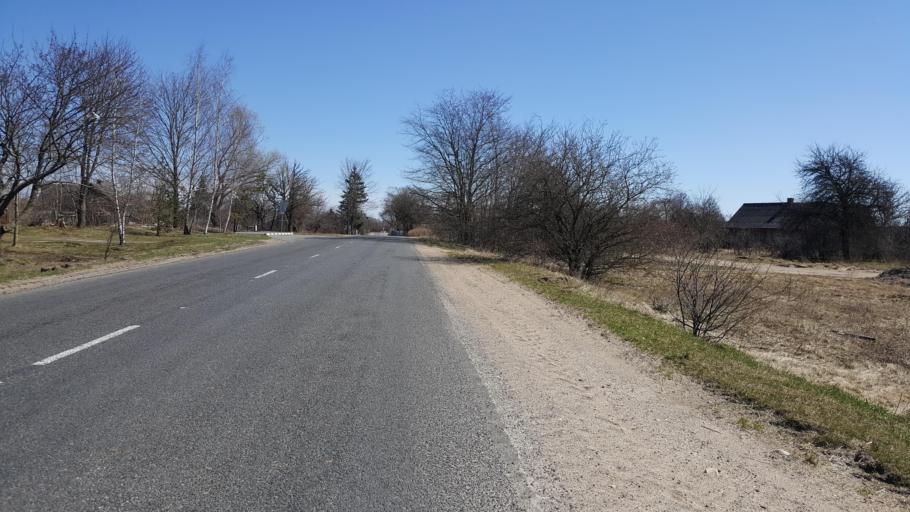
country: BY
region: Brest
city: Charnawchytsy
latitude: 52.2598
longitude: 23.8586
